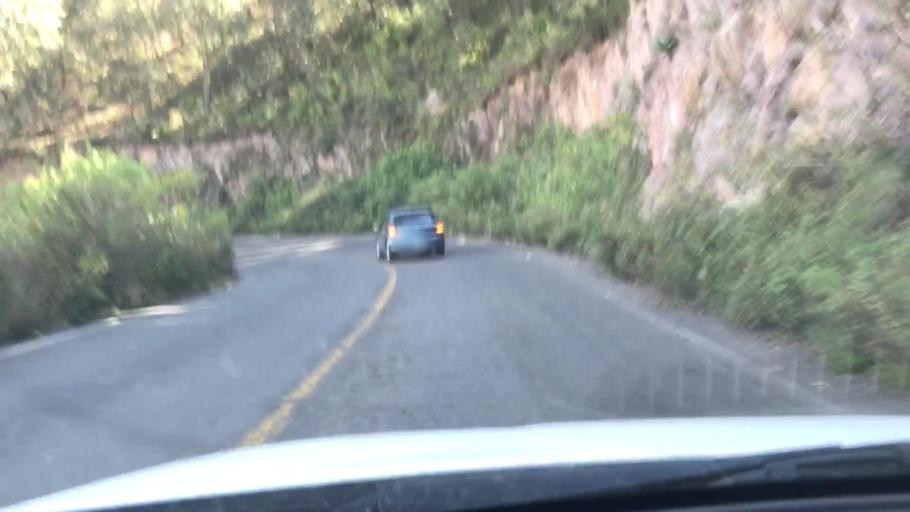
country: MX
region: Jalisco
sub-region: Zacoalco de Torres
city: Barranca de Otates (Barranca de Otatan)
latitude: 20.2015
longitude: -103.6935
